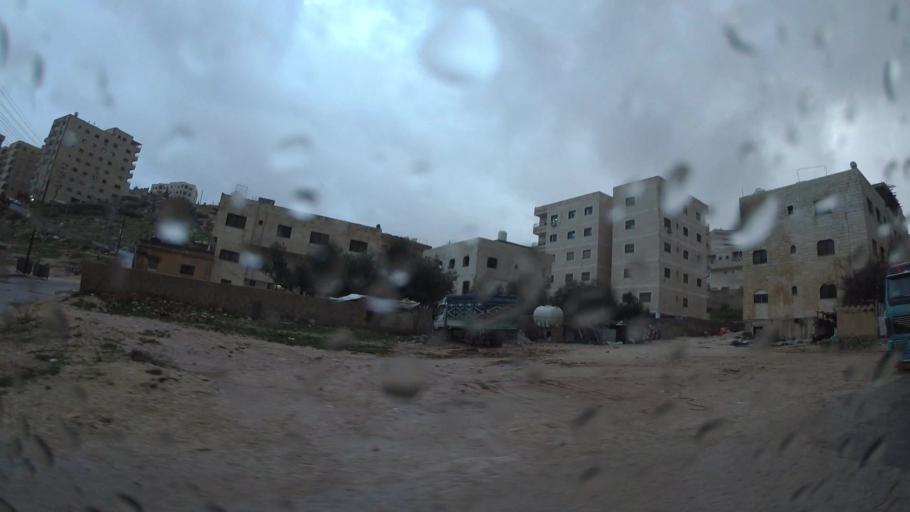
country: JO
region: Amman
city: Amman
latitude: 32.0023
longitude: 35.9231
